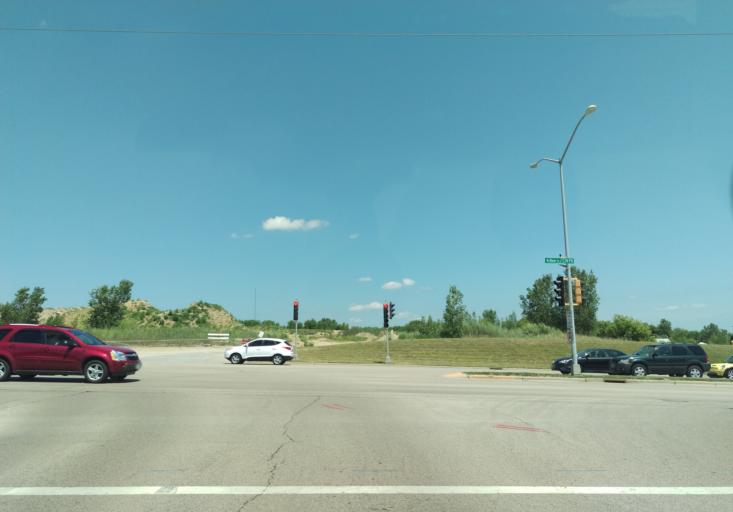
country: US
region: Wisconsin
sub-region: Dane County
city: Fitchburg
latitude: 43.0155
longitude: -89.4806
